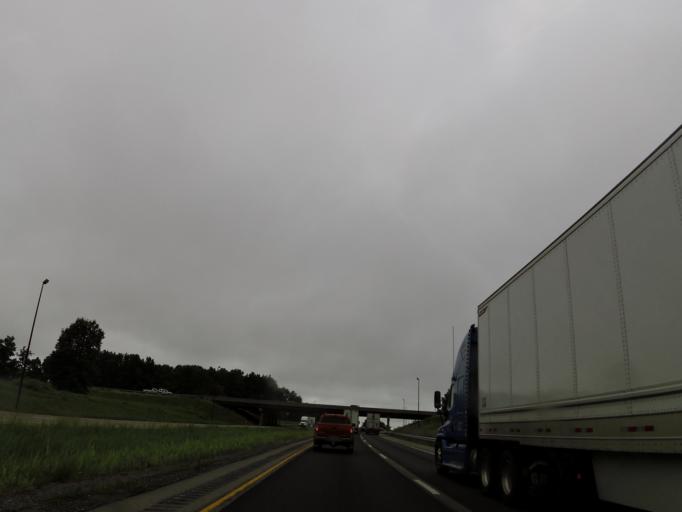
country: US
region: Illinois
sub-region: Franklin County
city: Benton
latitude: 37.9952
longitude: -88.9348
